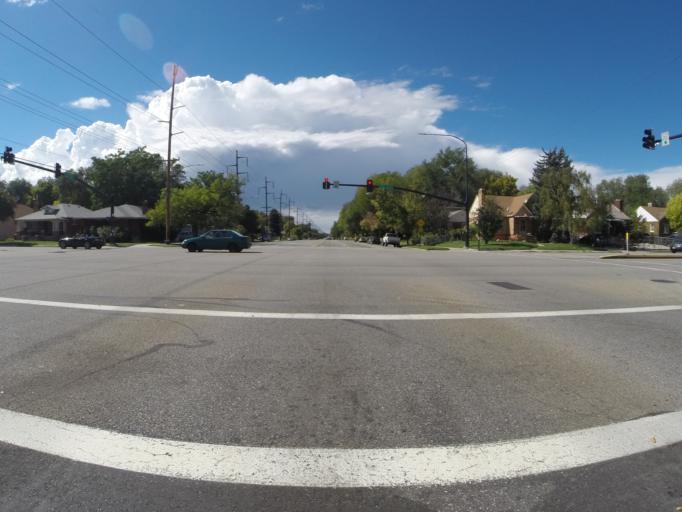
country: US
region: Utah
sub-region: Salt Lake County
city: Salt Lake City
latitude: 40.7520
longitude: -111.8709
